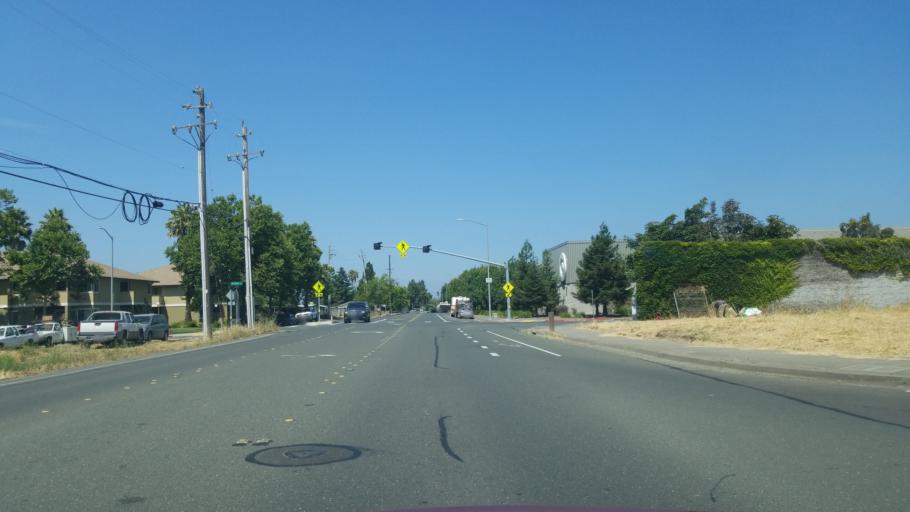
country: US
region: California
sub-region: Sonoma County
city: Roseland
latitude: 38.4165
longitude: -122.7074
